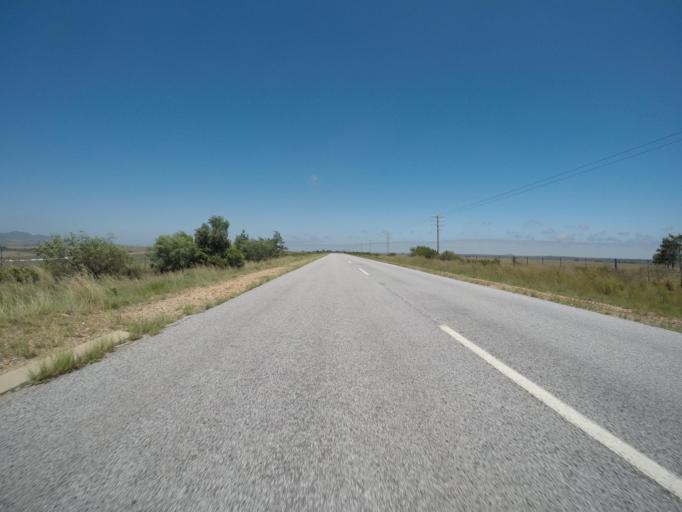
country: ZA
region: Eastern Cape
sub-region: Cacadu District Municipality
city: Kruisfontein
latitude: -34.0128
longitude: 24.5640
